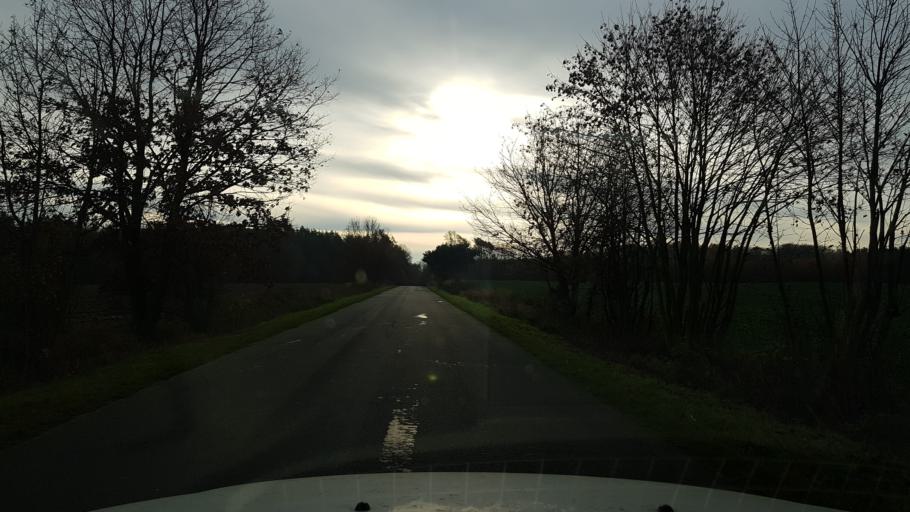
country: PL
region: West Pomeranian Voivodeship
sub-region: Powiat gryfinski
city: Banie
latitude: 53.0683
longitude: 14.6230
